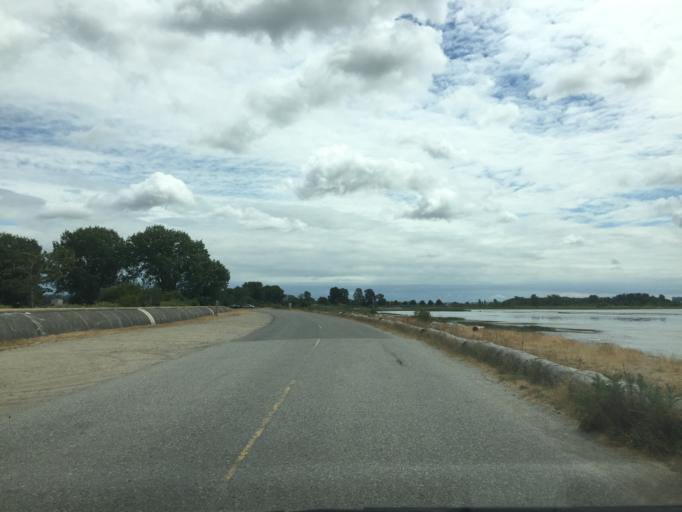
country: CA
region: British Columbia
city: Richmond
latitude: 49.2170
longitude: -123.2117
